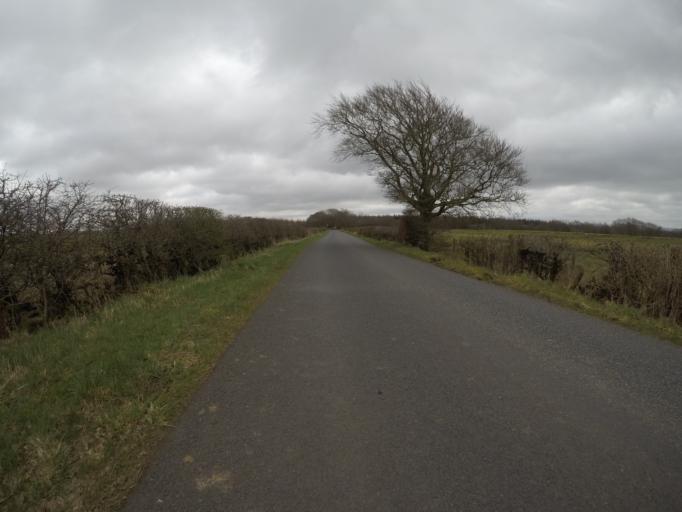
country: GB
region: Scotland
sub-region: East Ayrshire
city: Stewarton
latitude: 55.6812
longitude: -4.4435
